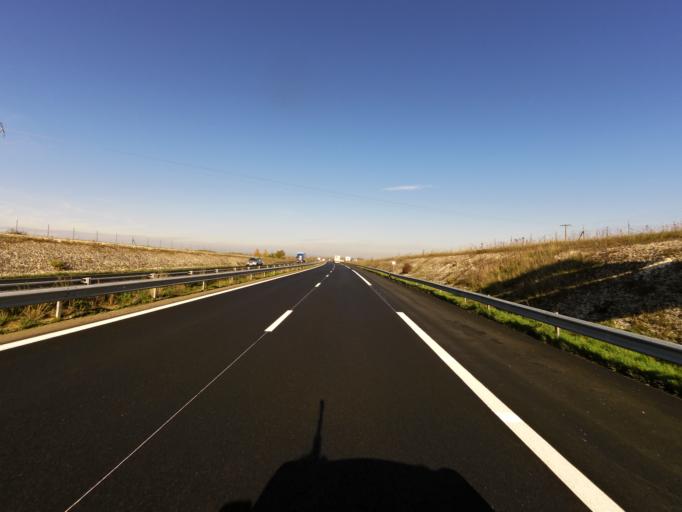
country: FR
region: Champagne-Ardenne
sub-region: Departement de la Marne
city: Fagnieres
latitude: 48.9581
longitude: 4.2880
